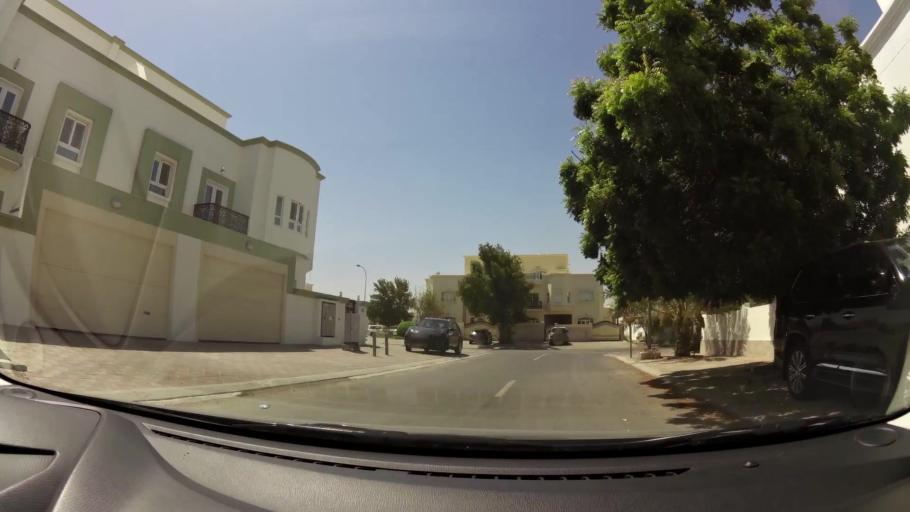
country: OM
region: Muhafazat Masqat
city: As Sib al Jadidah
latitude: 23.6256
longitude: 58.2528
